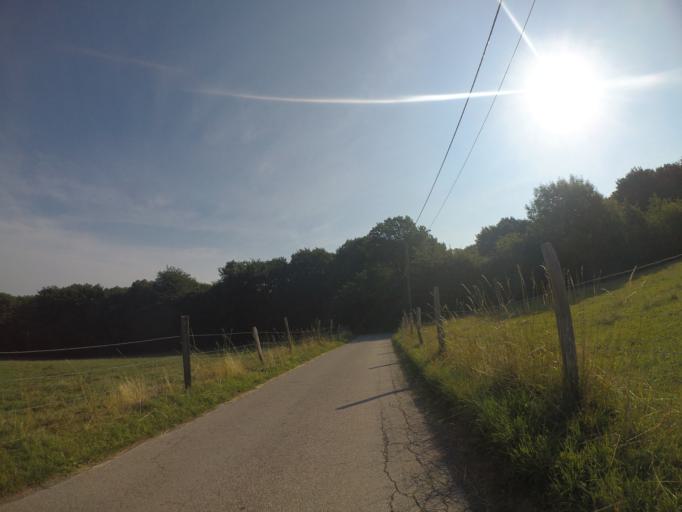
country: DE
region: North Rhine-Westphalia
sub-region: Regierungsbezirk Arnsberg
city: Schwelm
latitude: 51.2685
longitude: 7.2672
